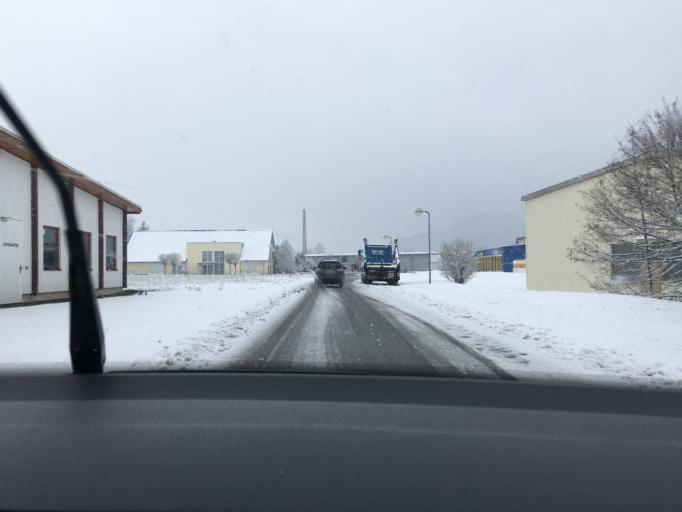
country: DE
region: Baden-Wuerttemberg
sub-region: Freiburg Region
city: Gottmadingen
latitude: 47.7356
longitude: 8.7902
